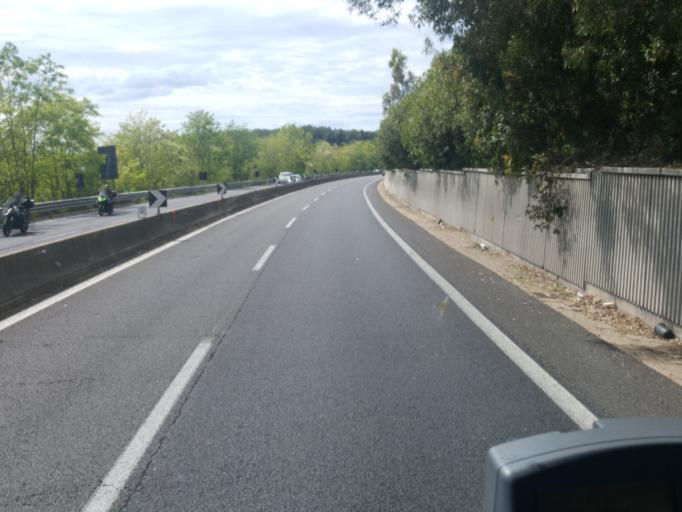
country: IT
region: Latium
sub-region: Citta metropolitana di Roma Capitale
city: Ara Nova
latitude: 41.8972
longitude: 12.2807
